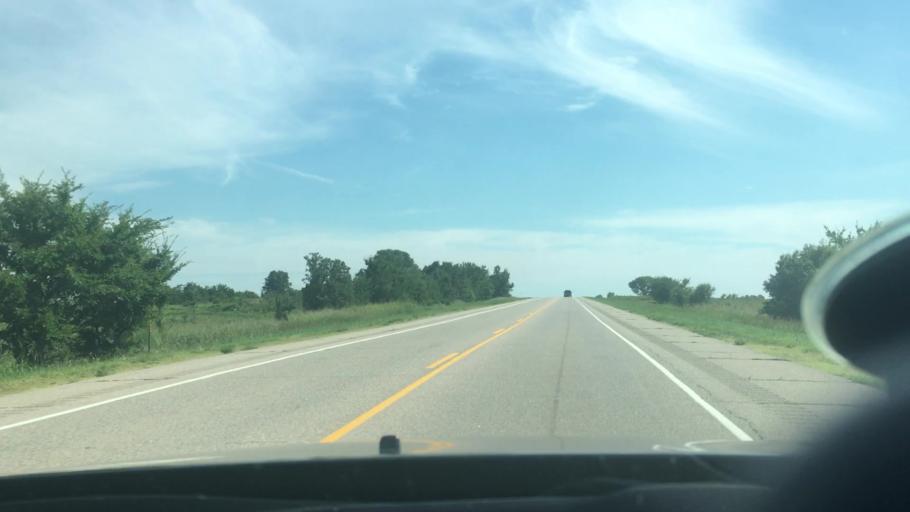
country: US
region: Oklahoma
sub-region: Seminole County
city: Maud
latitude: 35.0941
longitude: -96.6788
